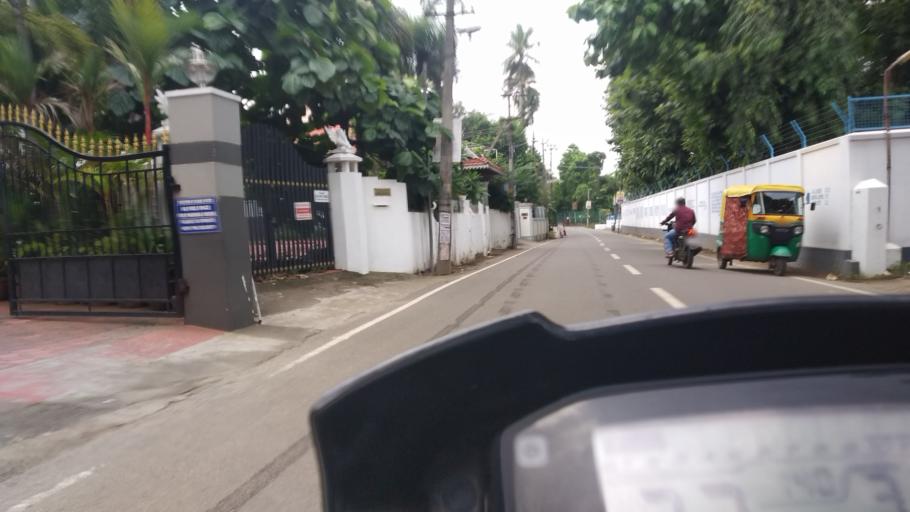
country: IN
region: Kerala
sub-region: Ernakulam
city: Aluva
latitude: 10.1142
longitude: 76.3470
